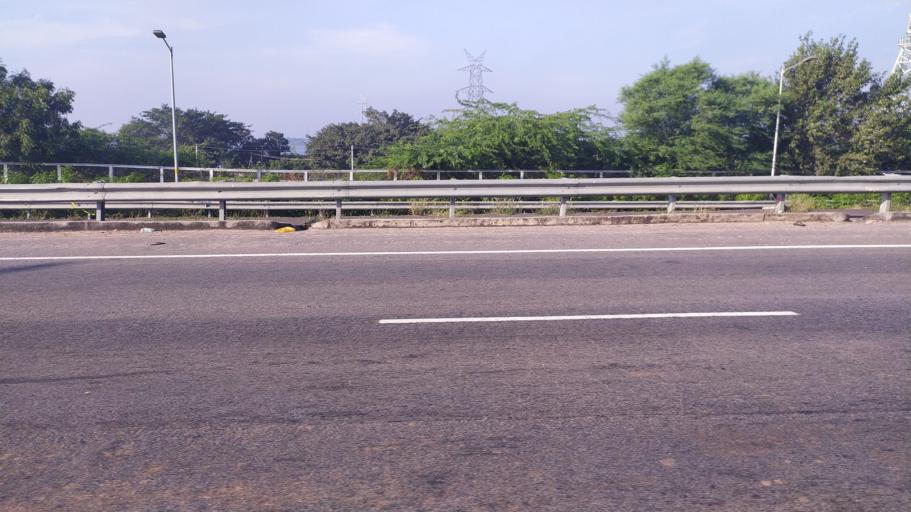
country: IN
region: Telangana
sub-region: Hyderabad
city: Hyderabad
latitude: 17.3464
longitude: 78.3616
